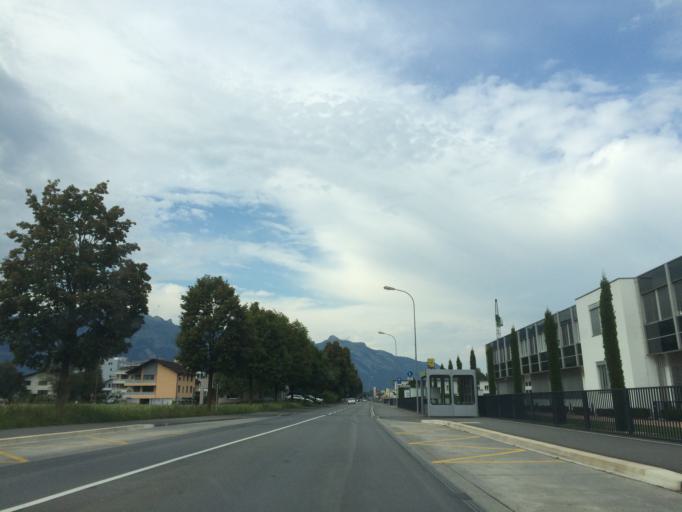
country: LI
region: Schaan
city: Schaan
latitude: 47.1718
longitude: 9.5090
